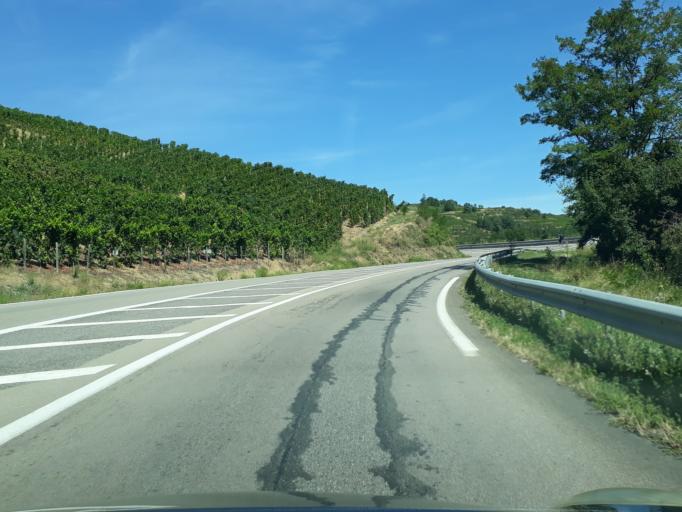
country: FR
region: Rhone-Alpes
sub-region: Departement de l'Ardeche
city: Andance
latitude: 45.2514
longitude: 4.7697
